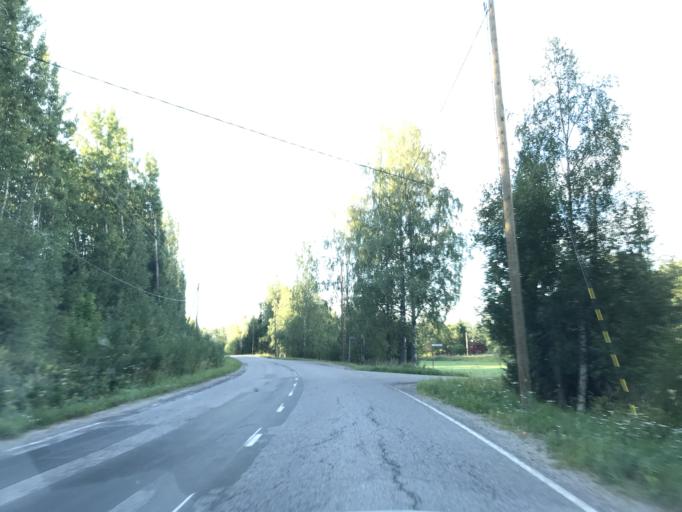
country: FI
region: Uusimaa
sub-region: Helsinki
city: Nurmijaervi
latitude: 60.3720
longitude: 24.6785
